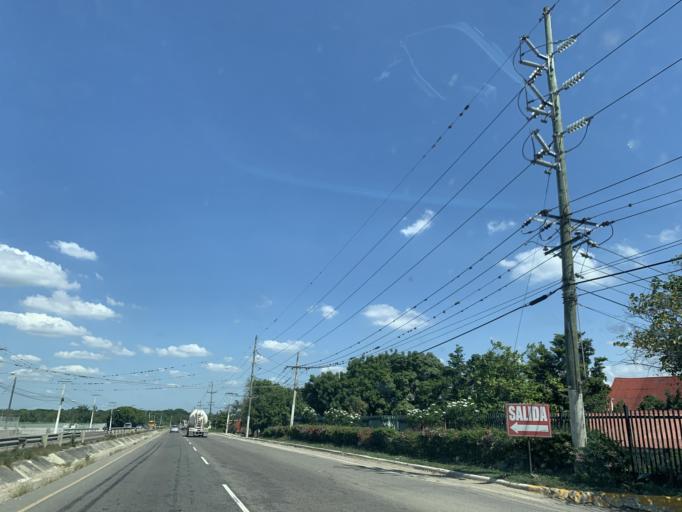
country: DO
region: Santiago
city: Villa Gonzalez
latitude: 19.5280
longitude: -70.7744
